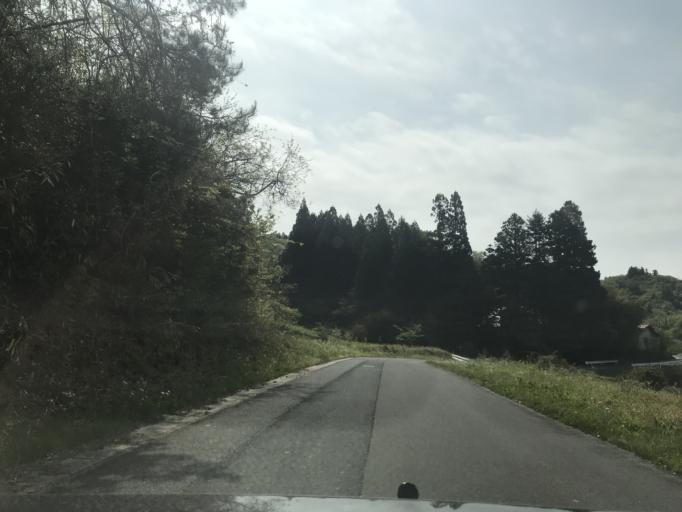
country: JP
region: Iwate
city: Ichinoseki
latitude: 38.8989
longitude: 141.0601
